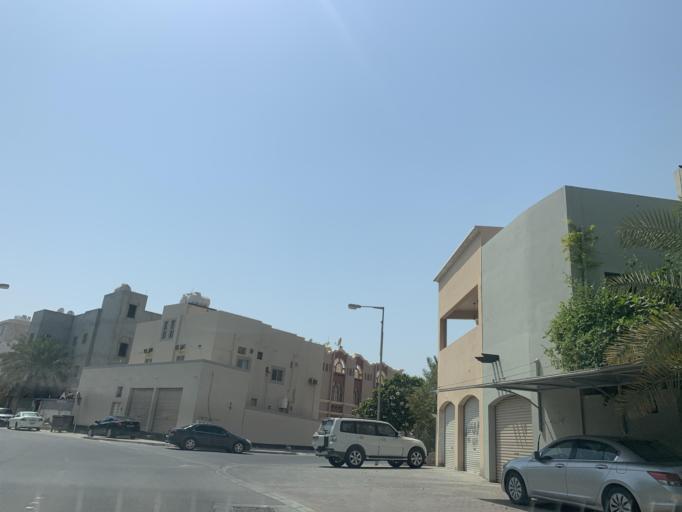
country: BH
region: Manama
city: Jidd Hafs
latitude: 26.2028
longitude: 50.5229
